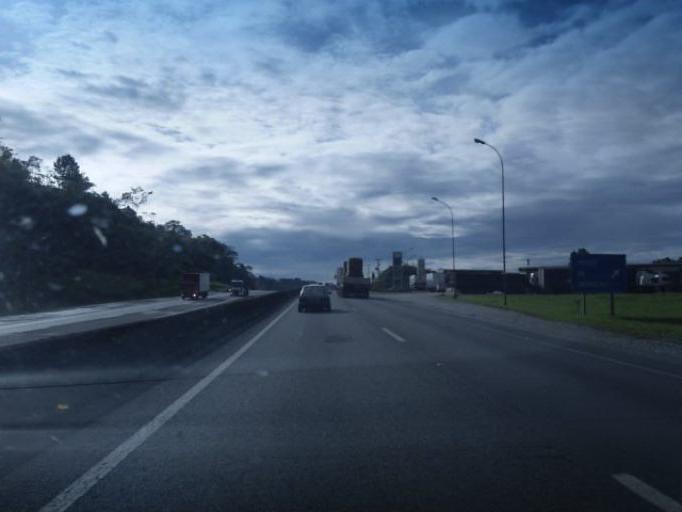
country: BR
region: Parana
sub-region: Antonina
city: Antonina
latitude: -25.1024
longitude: -48.7230
